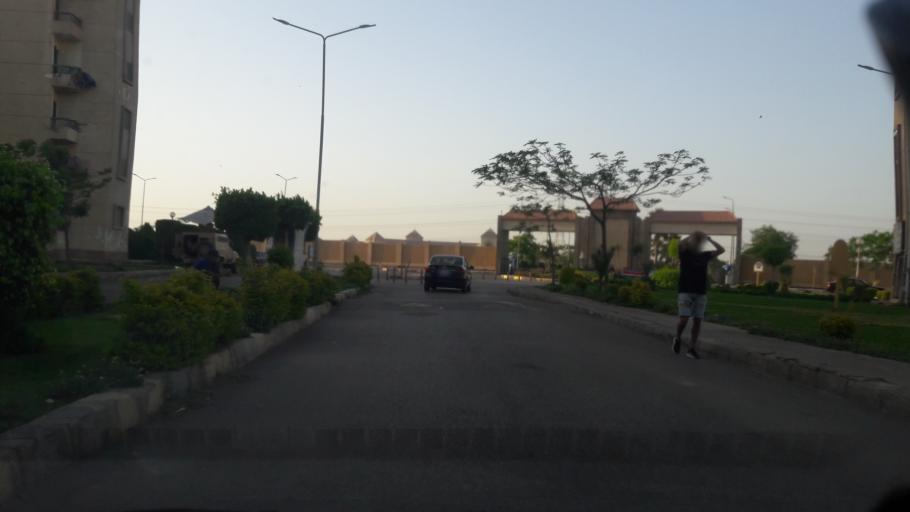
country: EG
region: Al Jizah
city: Madinat Sittah Uktubar
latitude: 29.9569
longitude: 31.0457
